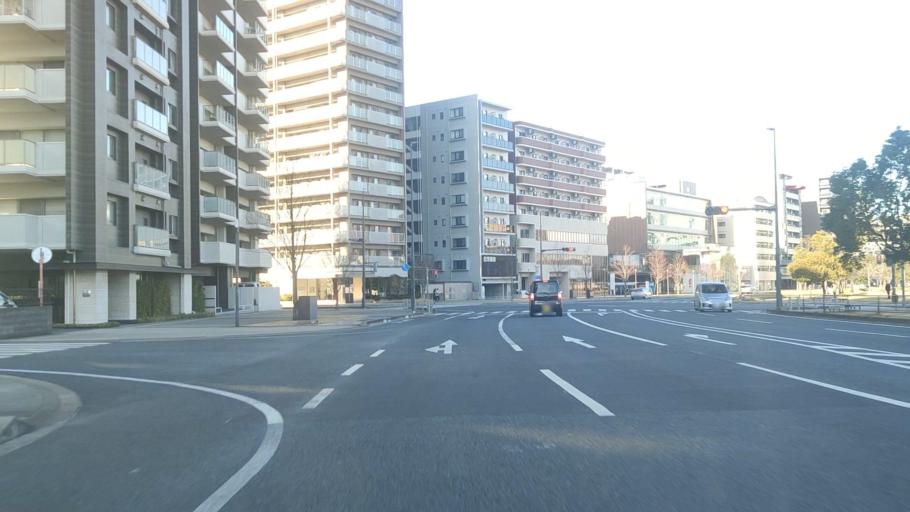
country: JP
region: Oita
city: Oita
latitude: 33.2291
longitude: 131.6034
